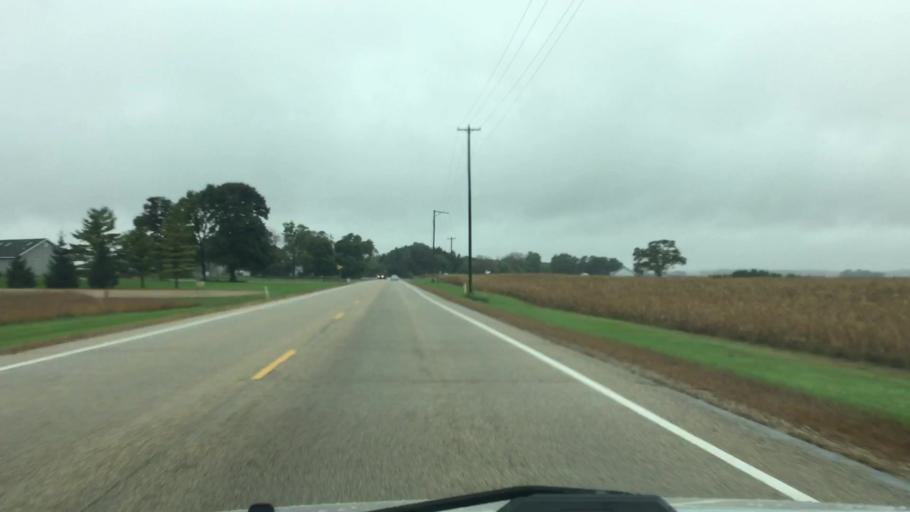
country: US
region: Wisconsin
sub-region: Jefferson County
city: Palmyra
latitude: 42.8777
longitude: -88.6327
